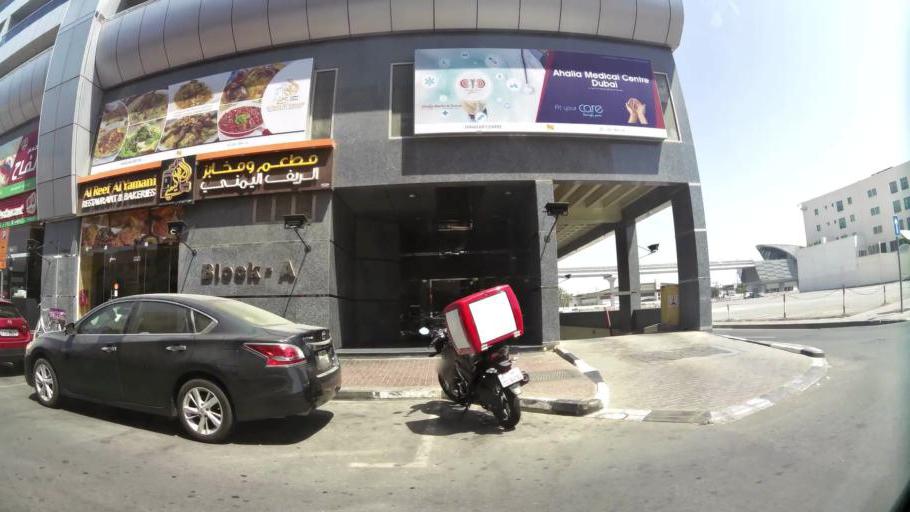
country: AE
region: Ash Shariqah
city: Sharjah
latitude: 25.2800
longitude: 55.3530
